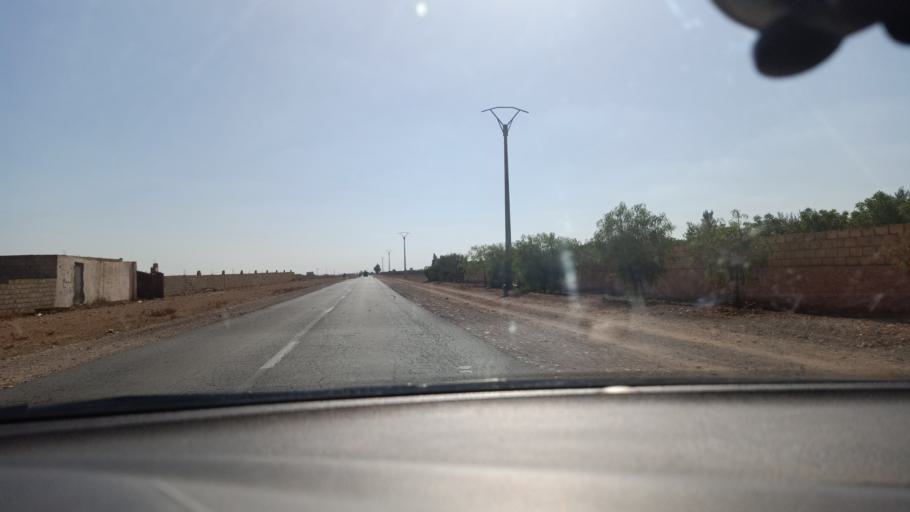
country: MA
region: Doukkala-Abda
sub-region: Safi
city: Youssoufia
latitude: 32.1286
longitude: -8.6003
